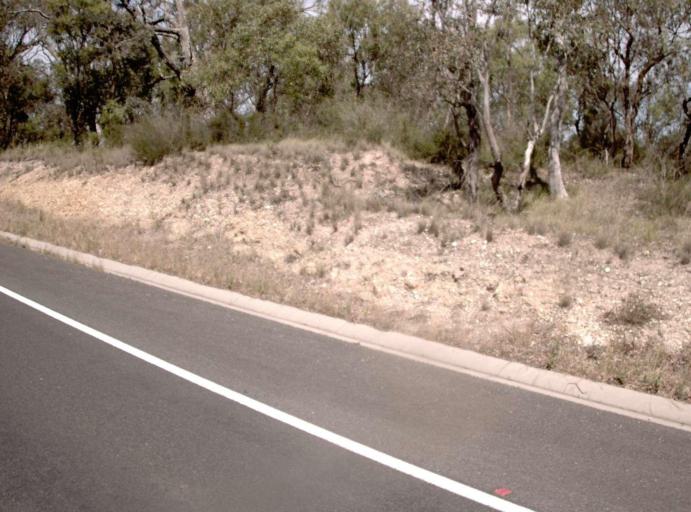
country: AU
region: Victoria
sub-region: East Gippsland
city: Bairnsdale
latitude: -37.8999
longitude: 147.3576
